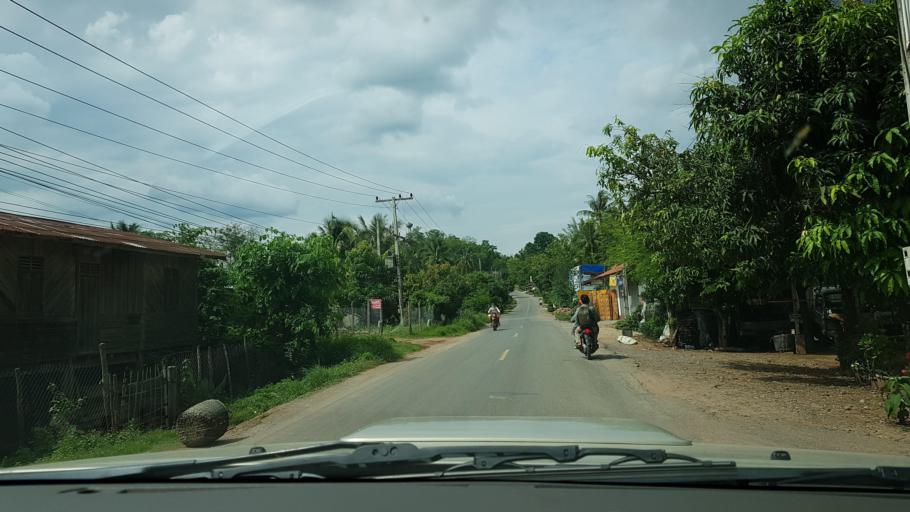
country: LA
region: Loungnamtha
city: Muang Nale
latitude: 20.3050
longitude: 101.6463
